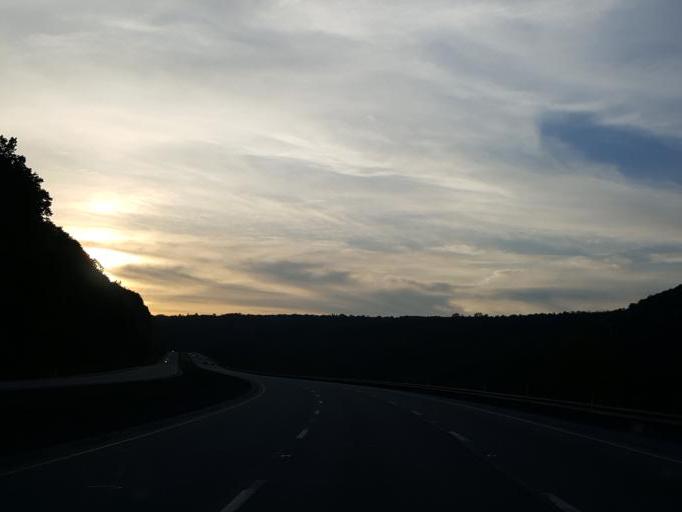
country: US
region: Pennsylvania
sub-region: Blair County
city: Duncansville
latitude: 40.4685
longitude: -78.4842
